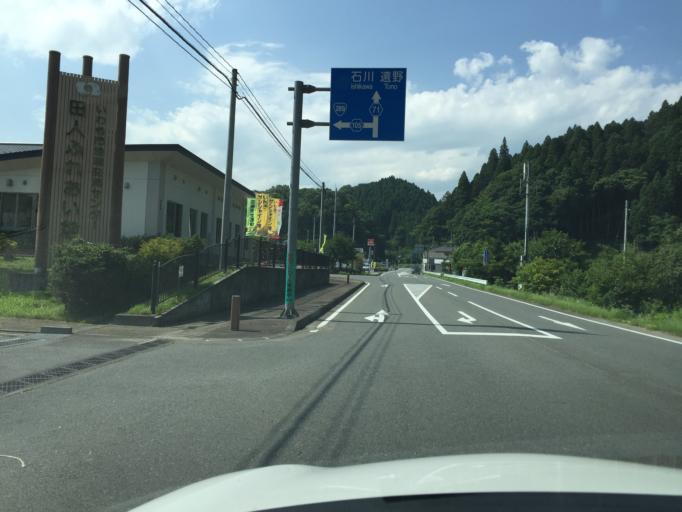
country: JP
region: Ibaraki
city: Kitaibaraki
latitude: 36.9520
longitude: 140.7057
